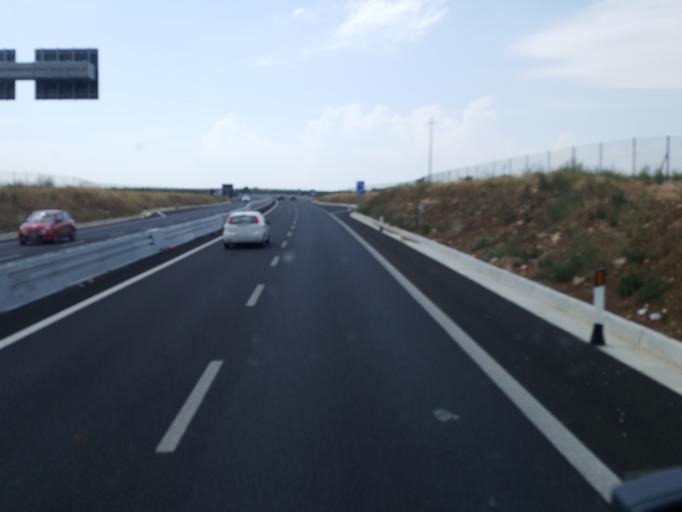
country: IT
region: Apulia
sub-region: Provincia di Bari
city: Palo del Colle
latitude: 41.0439
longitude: 16.7010
